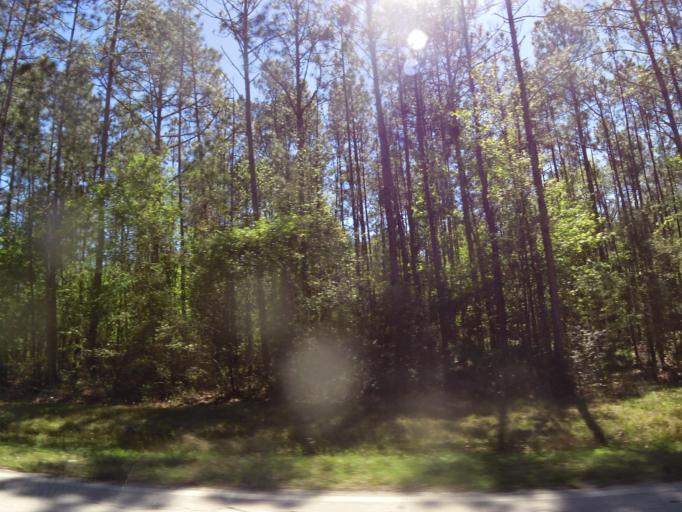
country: US
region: Florida
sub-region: Bradford County
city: Starke
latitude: 30.0559
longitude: -82.0628
